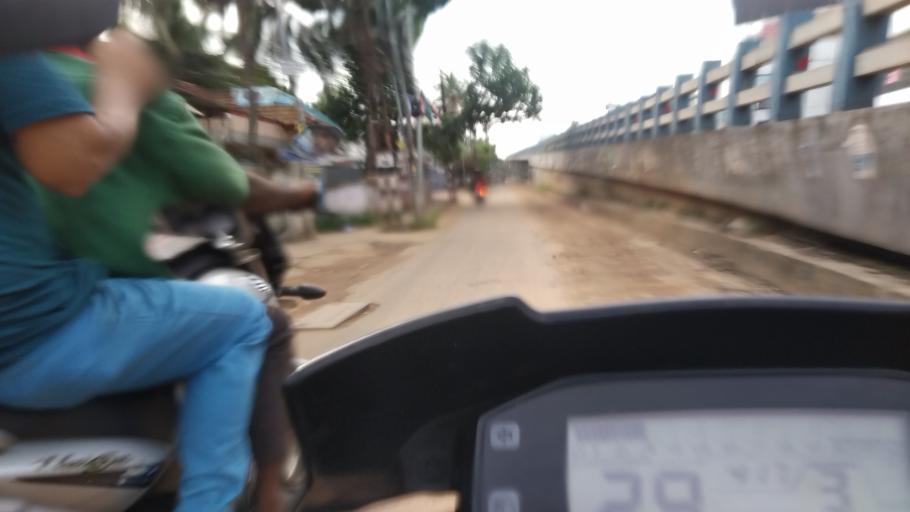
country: IN
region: Kerala
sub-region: Ernakulam
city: Cochin
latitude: 9.9734
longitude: 76.3162
